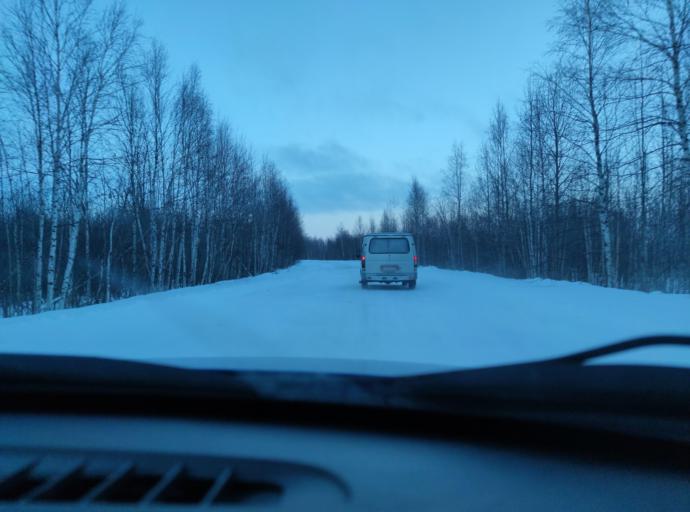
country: RU
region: Khanty-Mansiyskiy Avtonomnyy Okrug
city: Langepas
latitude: 61.1808
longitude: 75.1644
